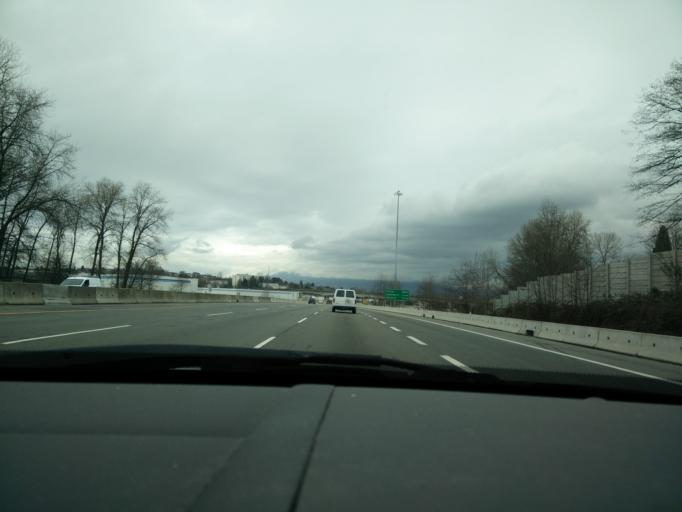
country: CA
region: British Columbia
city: Burnaby
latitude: 49.2594
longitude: -123.0211
